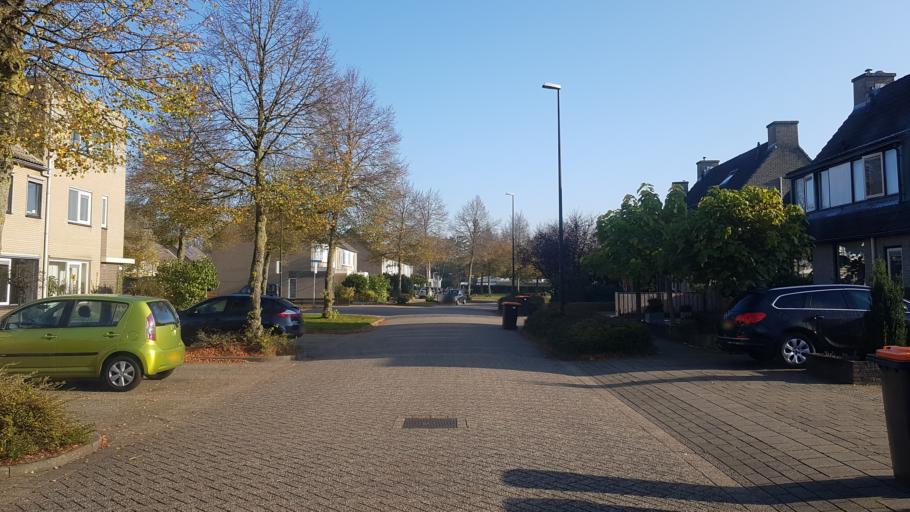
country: NL
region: Gelderland
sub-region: Gemeente Apeldoorn
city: Apeldoorn
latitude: 52.2173
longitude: 5.9962
